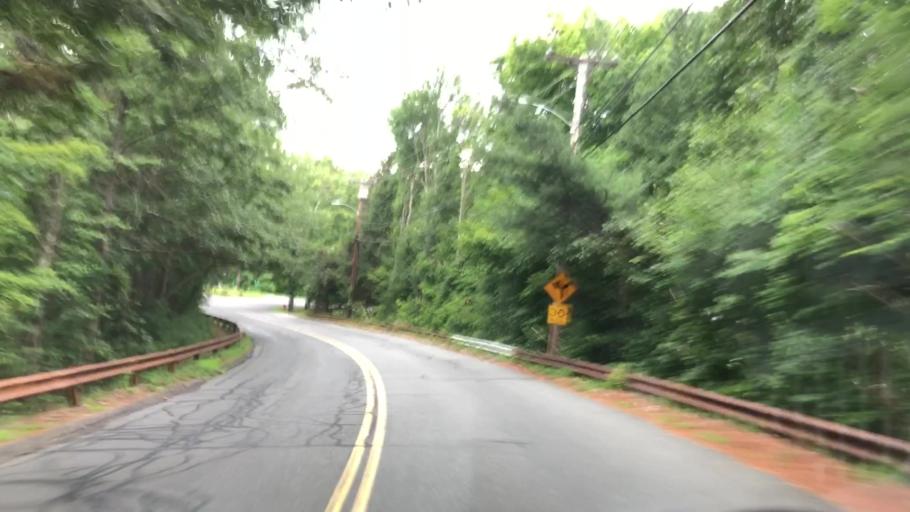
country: US
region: Massachusetts
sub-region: Hampden County
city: Holyoke
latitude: 42.1911
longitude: -72.6731
